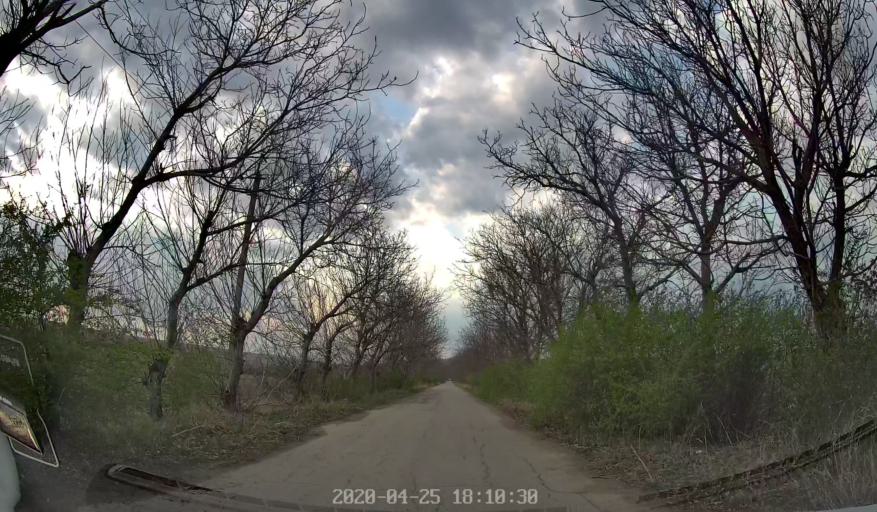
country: MD
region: Chisinau
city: Vadul lui Voda
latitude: 47.1340
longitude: 29.0764
